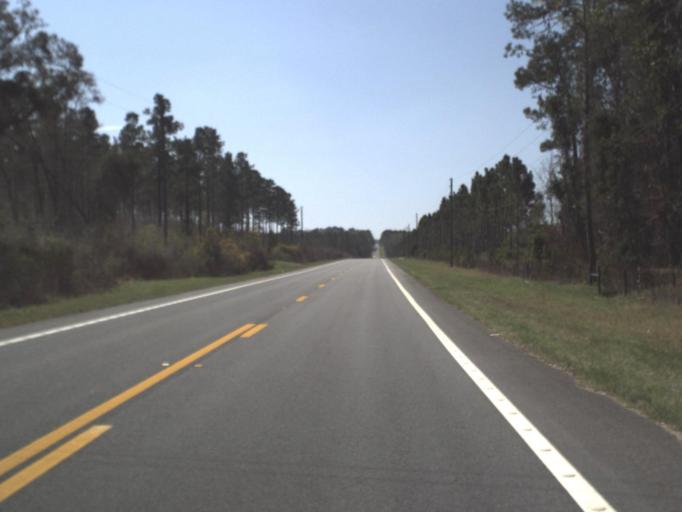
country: US
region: Florida
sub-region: Jefferson County
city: Monticello
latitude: 30.4503
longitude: -84.0187
